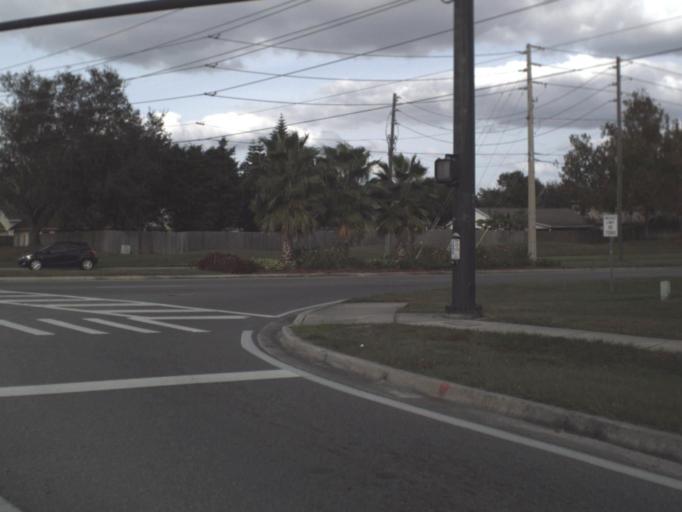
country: US
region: Florida
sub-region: Orange County
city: Williamsburg
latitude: 28.3967
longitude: -81.4249
